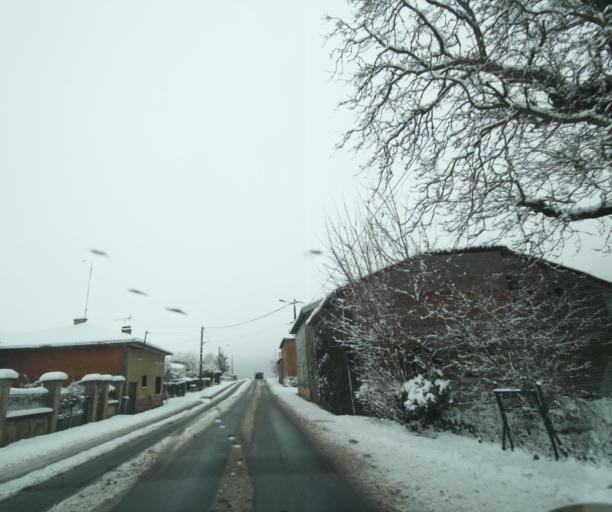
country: FR
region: Champagne-Ardenne
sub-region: Departement de la Haute-Marne
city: Wassy
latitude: 48.5476
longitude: 4.9242
